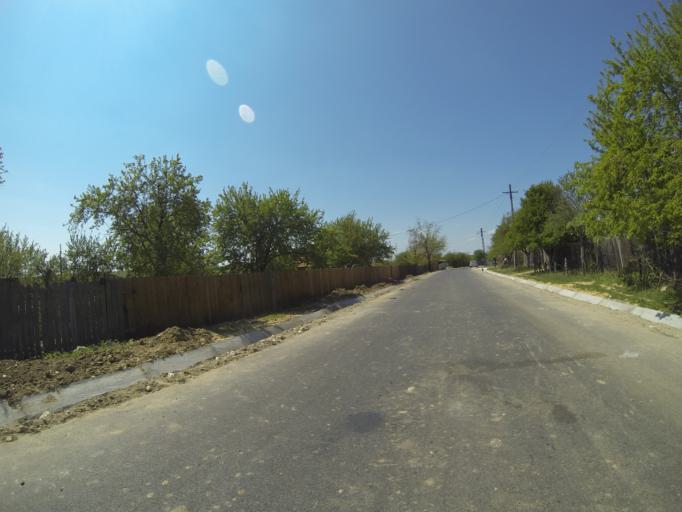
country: RO
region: Gorj
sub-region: Comuna Crusetu
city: Crusetu
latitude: 44.5881
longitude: 23.6588
